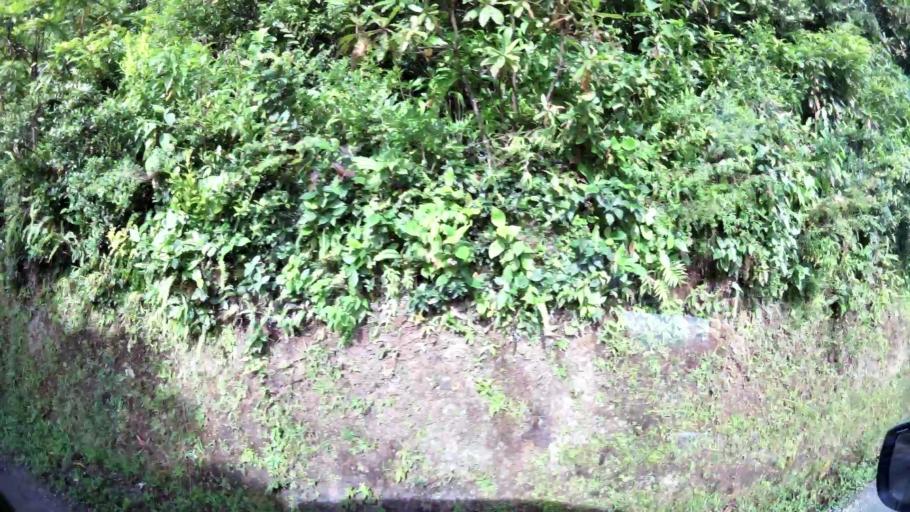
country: CR
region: Guanacaste
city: Juntas
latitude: 10.2997
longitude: -84.7973
